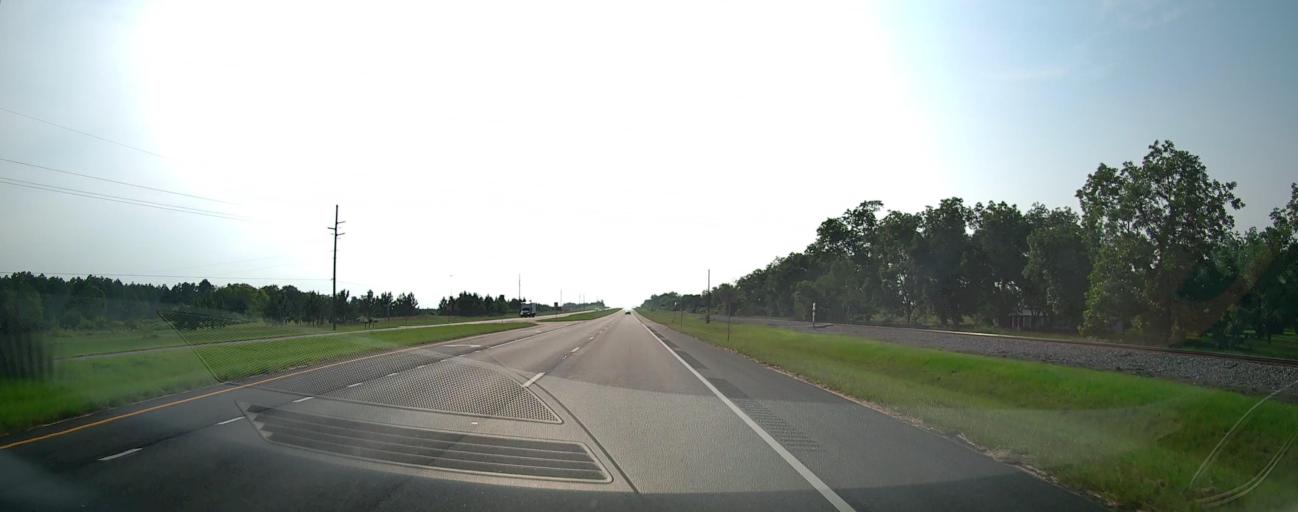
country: US
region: Georgia
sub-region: Taylor County
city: Butler
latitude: 32.5761
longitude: -84.3053
